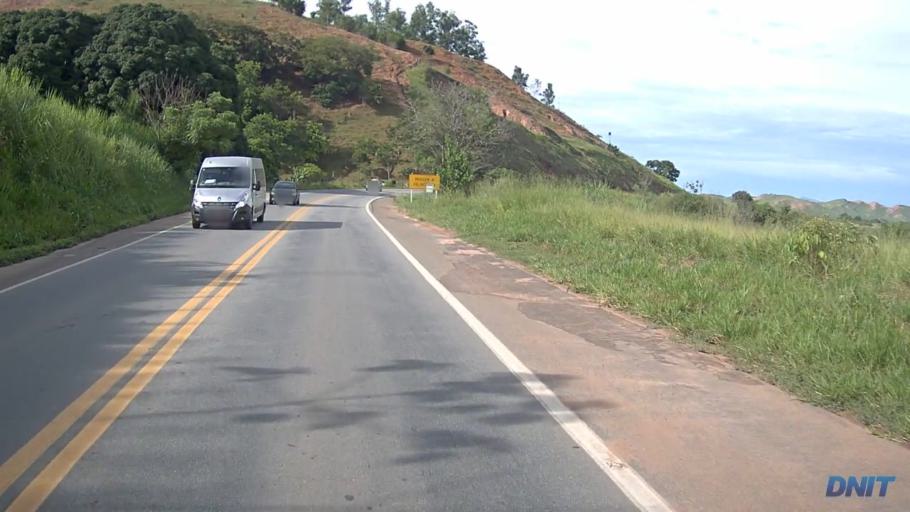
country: BR
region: Minas Gerais
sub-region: Belo Oriente
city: Belo Oriente
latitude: -19.1631
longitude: -42.2415
